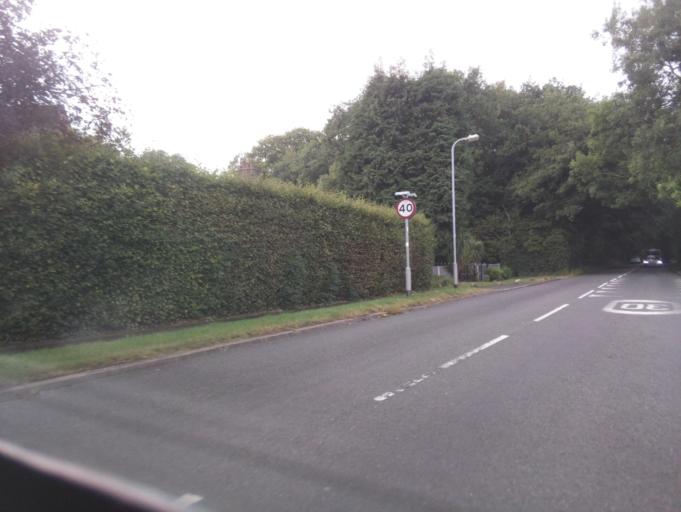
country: GB
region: England
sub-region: Staffordshire
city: Newcastle under Lyme
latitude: 52.9711
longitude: -2.2087
